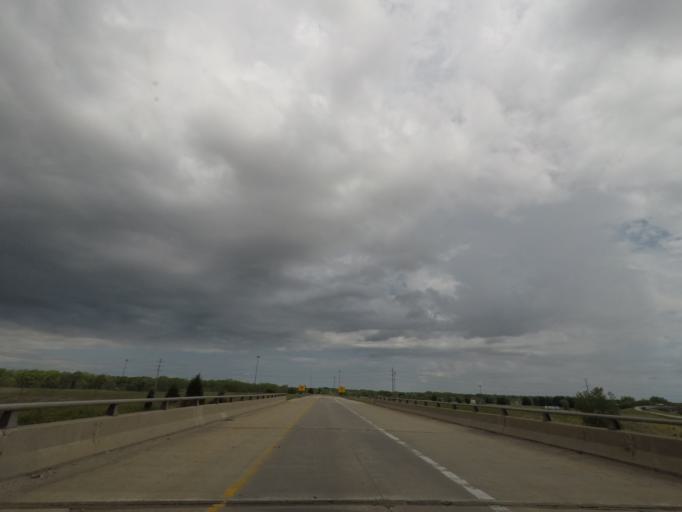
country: US
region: Illinois
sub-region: Winnebago County
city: Cherry Valley
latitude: 42.2165
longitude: -89.0113
